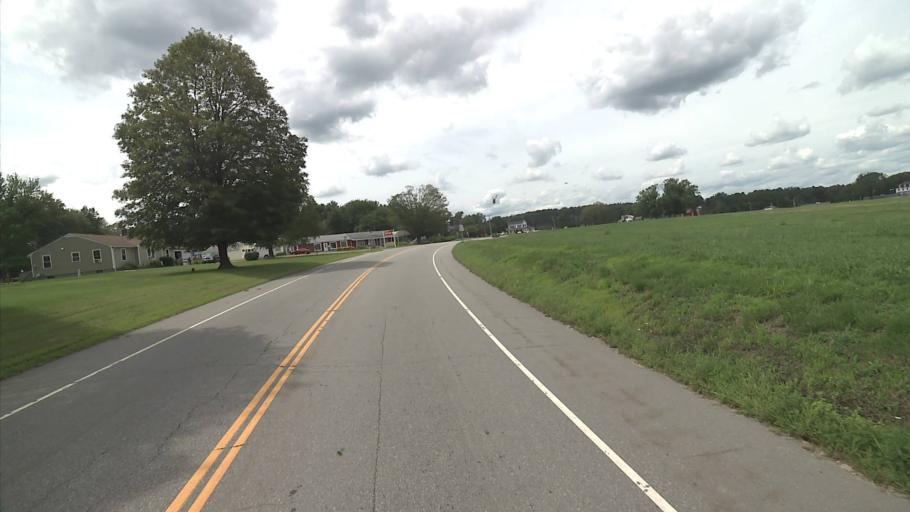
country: US
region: Connecticut
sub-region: Windham County
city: South Woodstock
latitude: 41.9328
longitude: -71.9540
